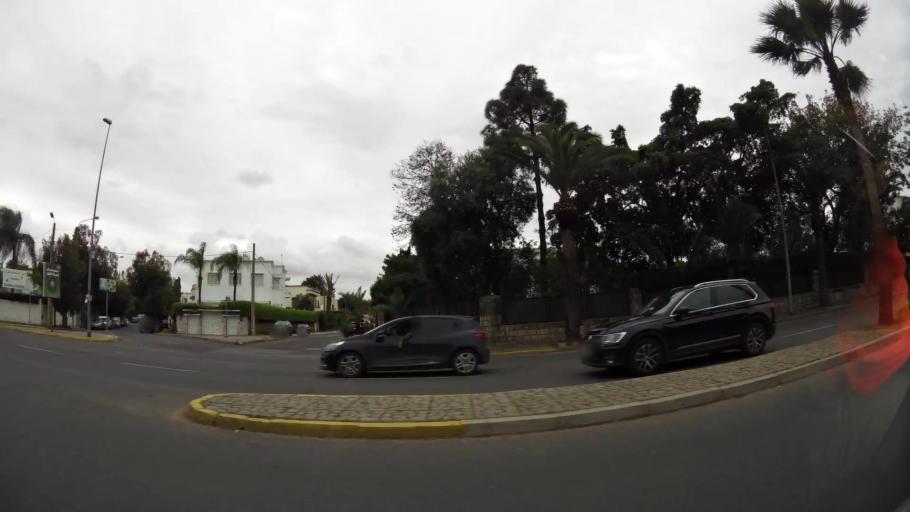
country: MA
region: Grand Casablanca
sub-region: Casablanca
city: Casablanca
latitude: 33.5621
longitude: -7.6201
